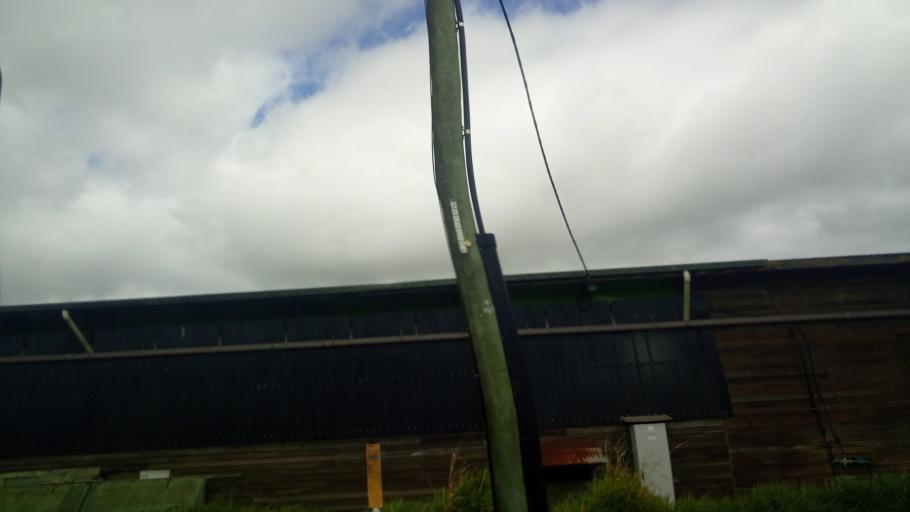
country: AU
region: Queensland
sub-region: Tablelands
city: Tolga
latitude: -17.2166
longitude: 145.5404
